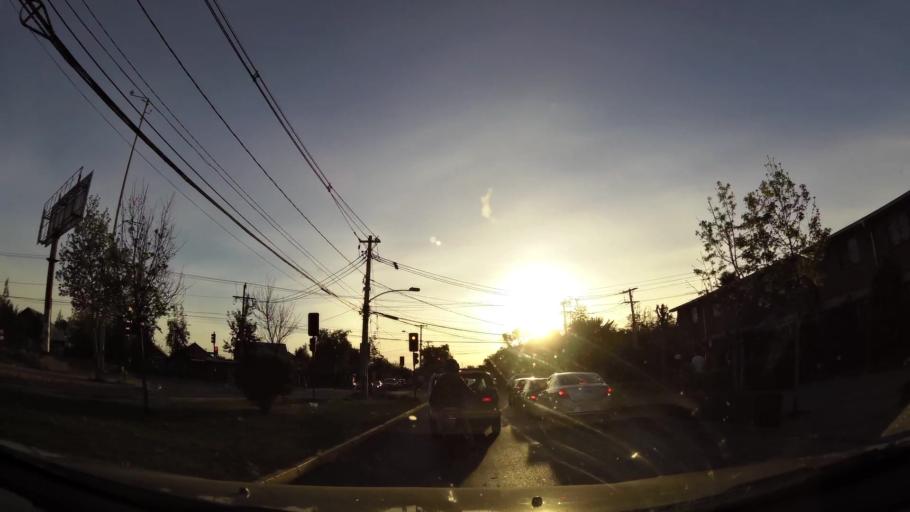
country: CL
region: Santiago Metropolitan
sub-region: Provincia de Cordillera
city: Puente Alto
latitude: -33.5964
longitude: -70.5575
